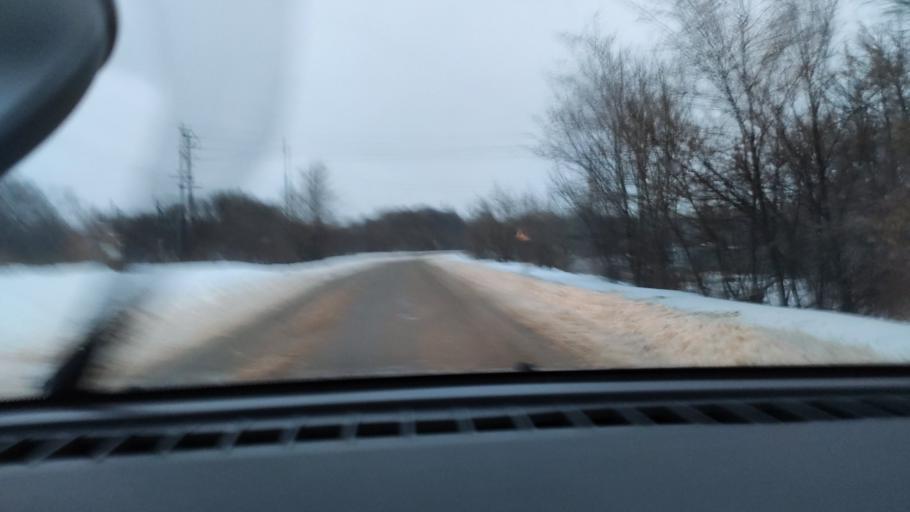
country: RU
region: Samara
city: Samara
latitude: 53.1288
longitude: 50.2366
